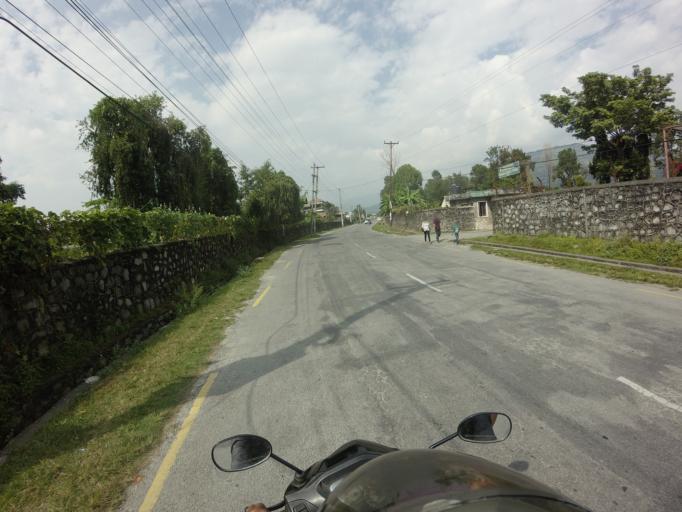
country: NP
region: Western Region
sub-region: Gandaki Zone
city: Pokhara
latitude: 28.2141
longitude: 83.9982
